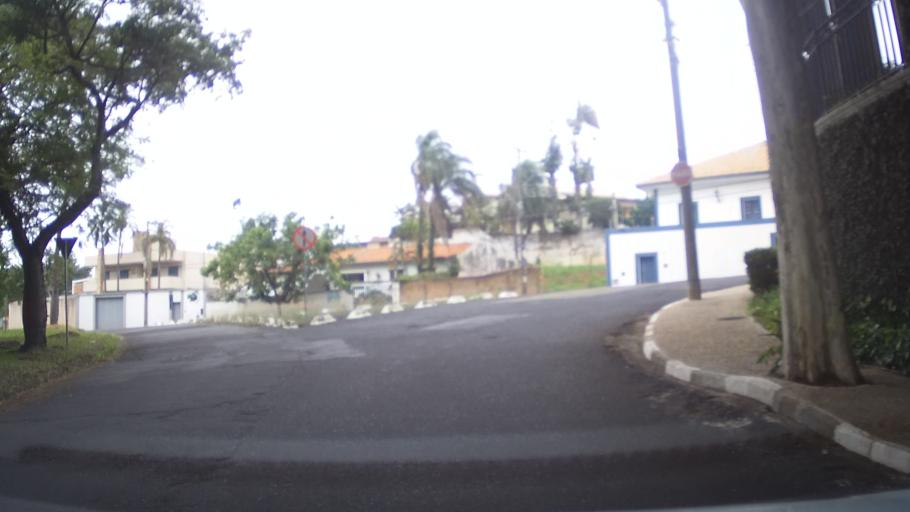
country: BR
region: Sao Paulo
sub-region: Campinas
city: Campinas
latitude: -22.9078
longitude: -47.0351
